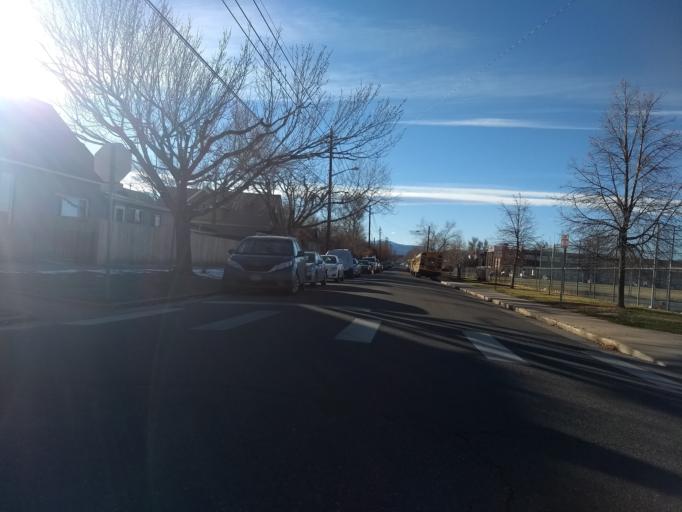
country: US
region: Colorado
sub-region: Denver County
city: Denver
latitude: 39.7242
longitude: -104.9929
